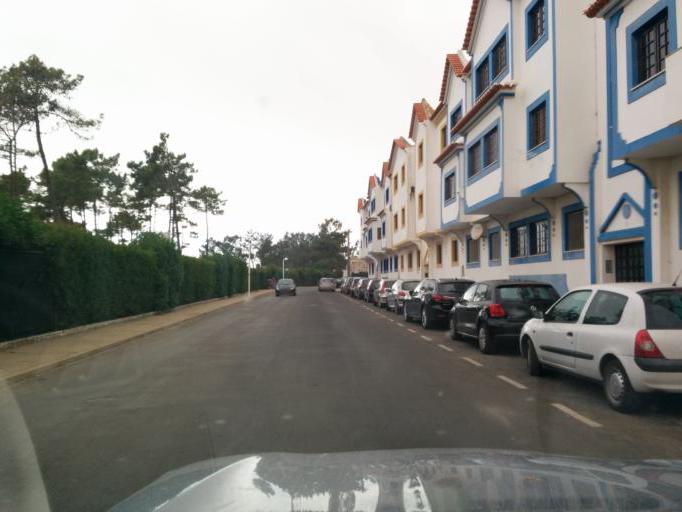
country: PT
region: Beja
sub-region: Odemira
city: Vila Nova de Milfontes
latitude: 37.7298
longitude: -8.7826
